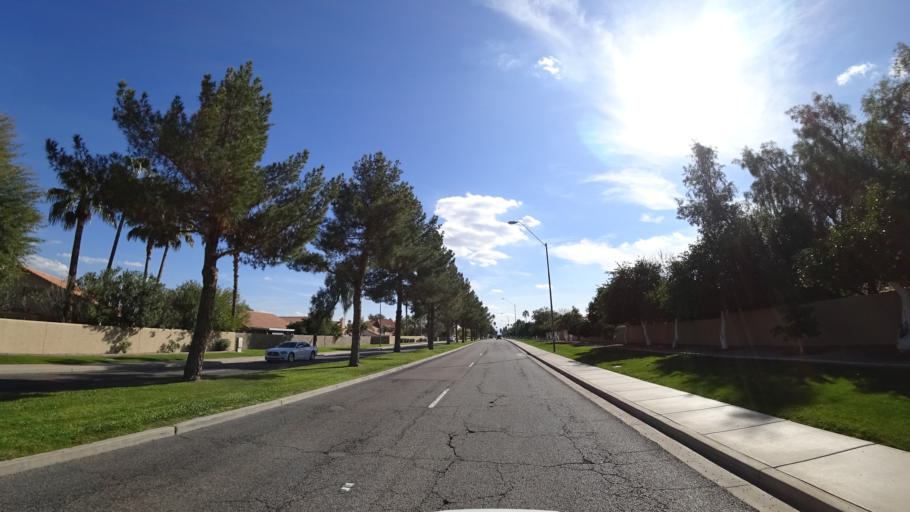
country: US
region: Arizona
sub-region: Maricopa County
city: Sun City
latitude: 33.6590
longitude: -112.2205
